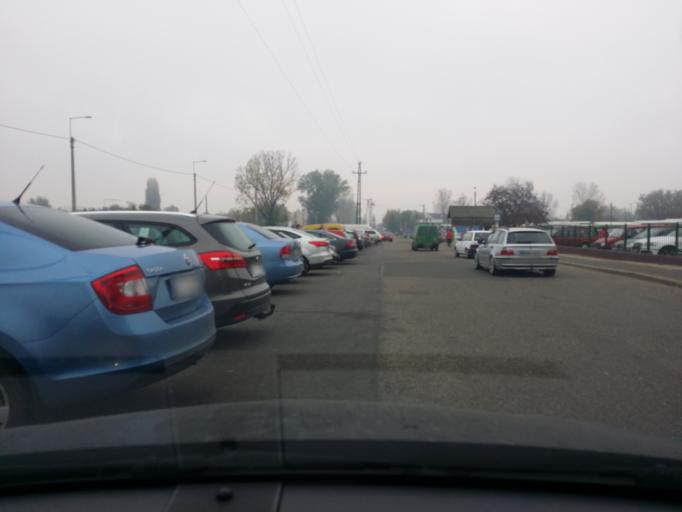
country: HU
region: Szabolcs-Szatmar-Bereg
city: Nyiregyhaza
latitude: 47.9699
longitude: 21.6940
